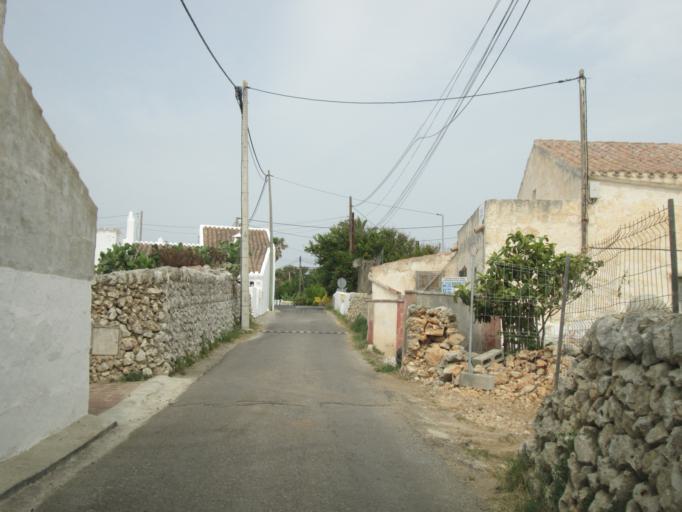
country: ES
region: Balearic Islands
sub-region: Illes Balears
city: Sant Lluis
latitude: 39.8420
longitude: 4.2478
